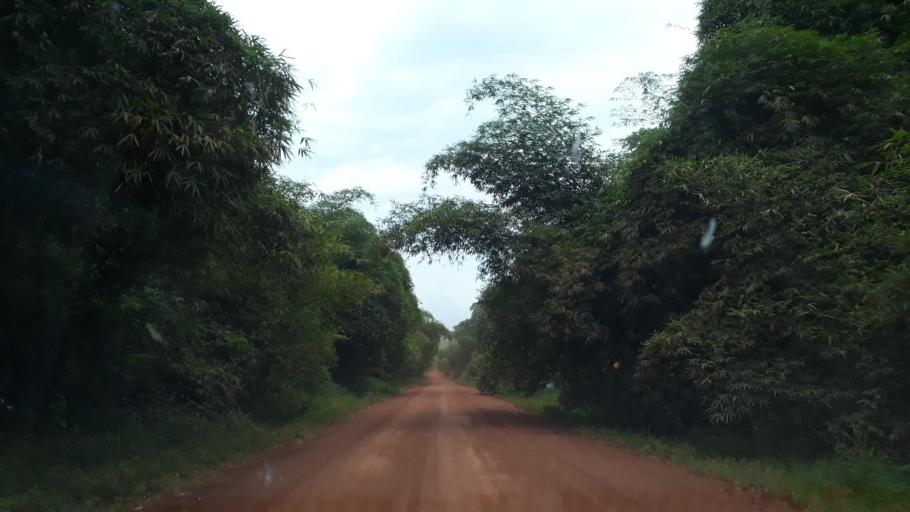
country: CD
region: Eastern Province
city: Kisangani
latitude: 0.6302
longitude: 26.0782
